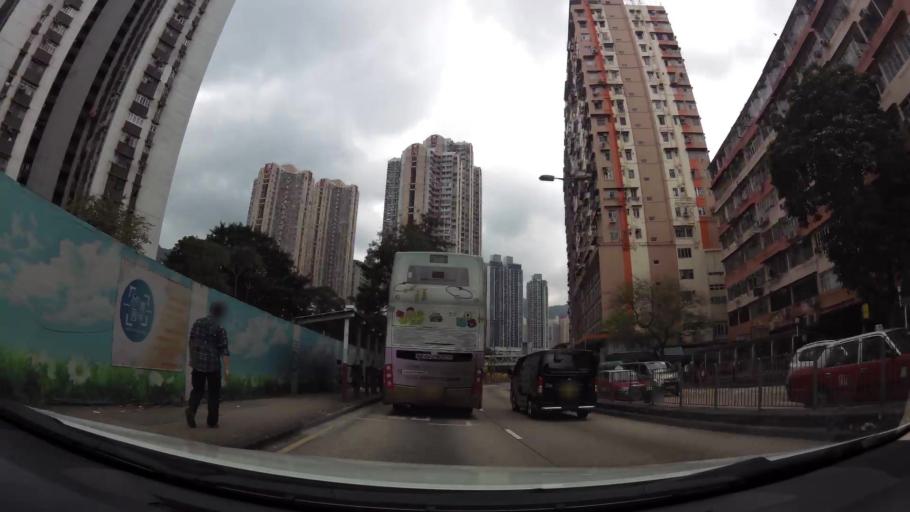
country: HK
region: Wong Tai Sin
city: Wong Tai Sin
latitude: 22.3357
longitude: 114.1943
